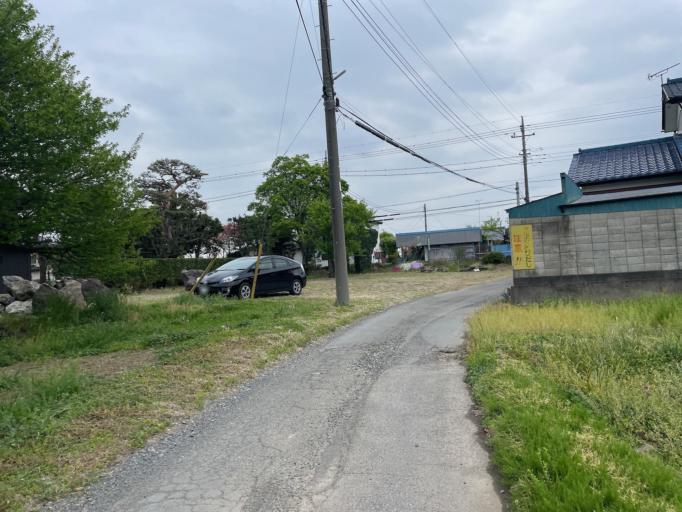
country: JP
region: Gunma
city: Sakai-nakajima
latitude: 36.2717
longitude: 139.2252
